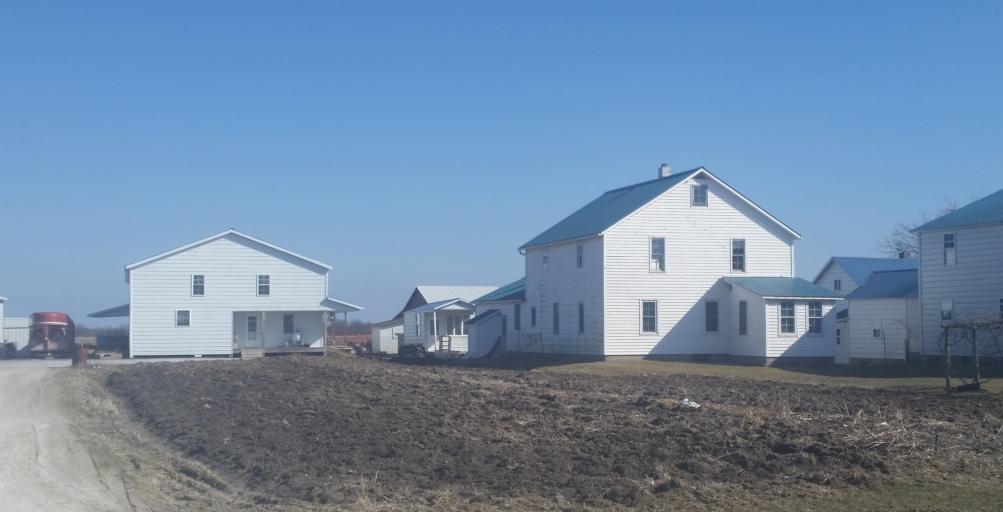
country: US
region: Missouri
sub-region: Randolph County
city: Moberly
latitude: 39.3361
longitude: -92.2973
